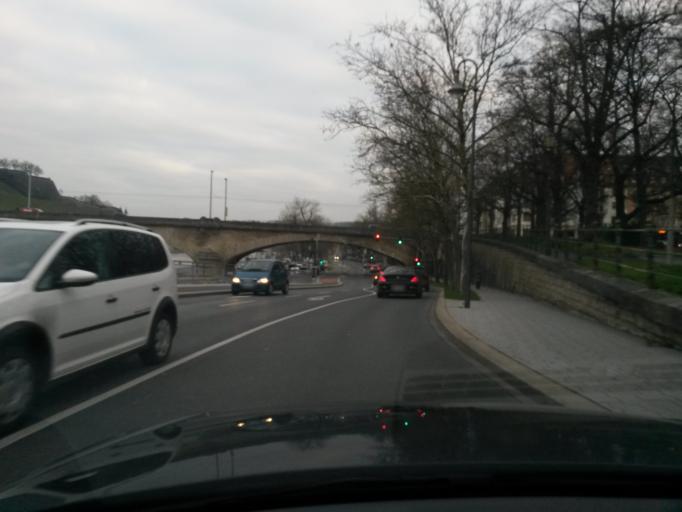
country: DE
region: Bavaria
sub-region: Regierungsbezirk Unterfranken
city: Wuerzburg
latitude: 49.7855
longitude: 9.9281
